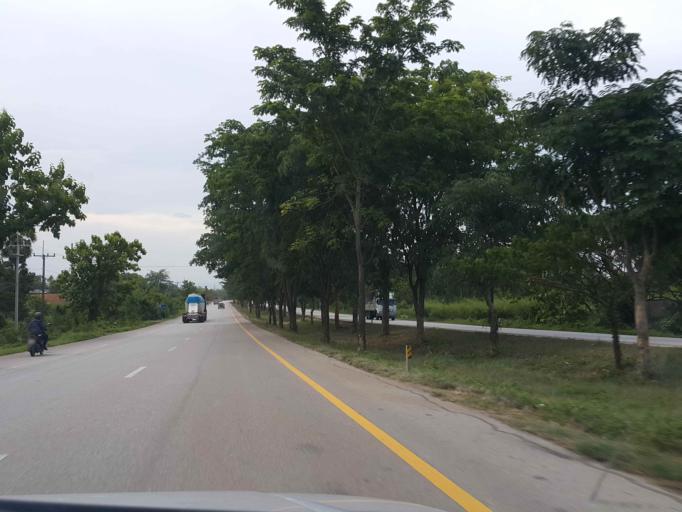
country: TH
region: Lampang
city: Ko Kha
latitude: 18.1358
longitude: 99.3905
